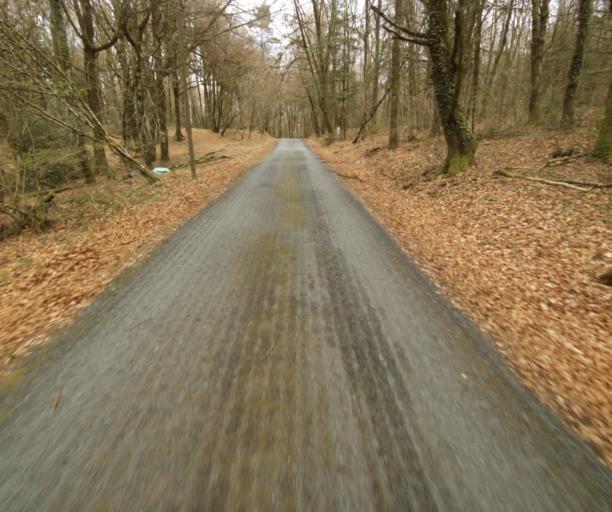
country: FR
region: Limousin
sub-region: Departement de la Correze
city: Egletons
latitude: 45.3938
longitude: 1.9623
